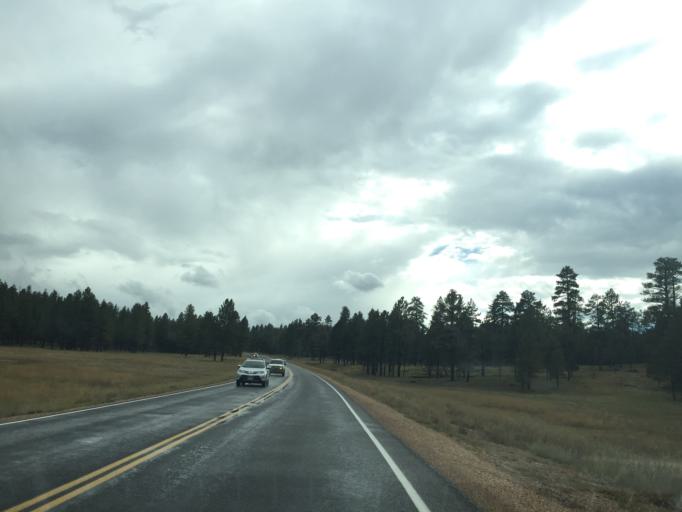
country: US
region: Utah
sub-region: Garfield County
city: Panguitch
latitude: 37.6375
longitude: -112.1714
